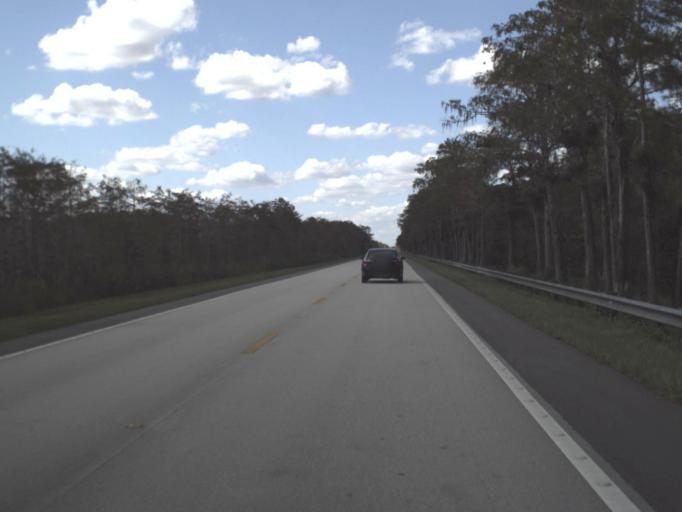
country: US
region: Florida
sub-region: Miami-Dade County
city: Kendall West
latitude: 25.8294
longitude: -80.9010
